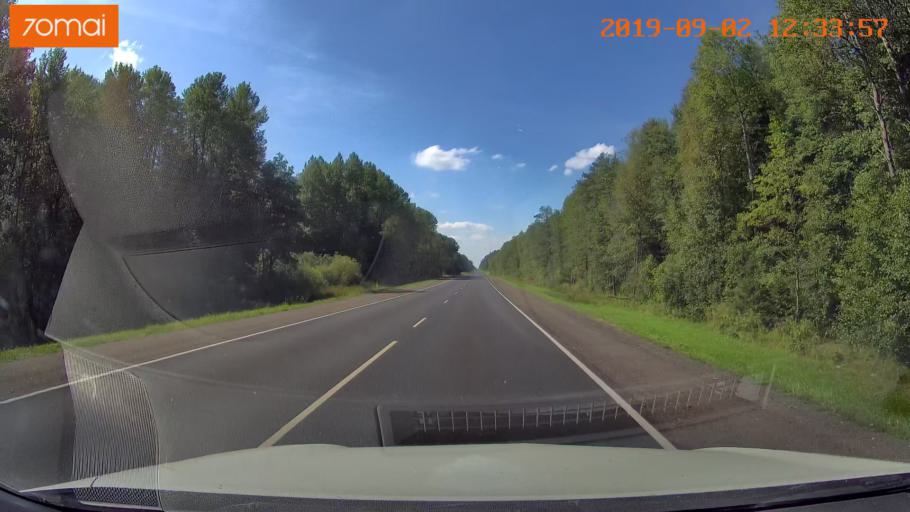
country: RU
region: Smolensk
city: Shumyachi
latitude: 53.8139
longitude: 32.4159
